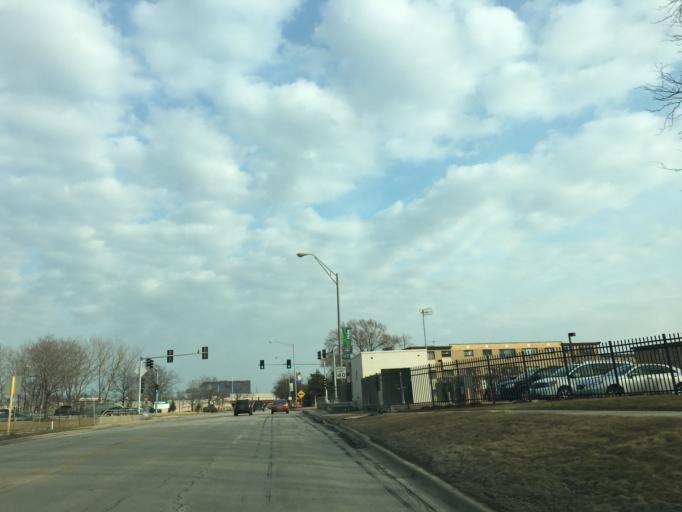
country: US
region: Illinois
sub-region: Cook County
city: Rosemont
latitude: 41.9971
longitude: -87.8801
